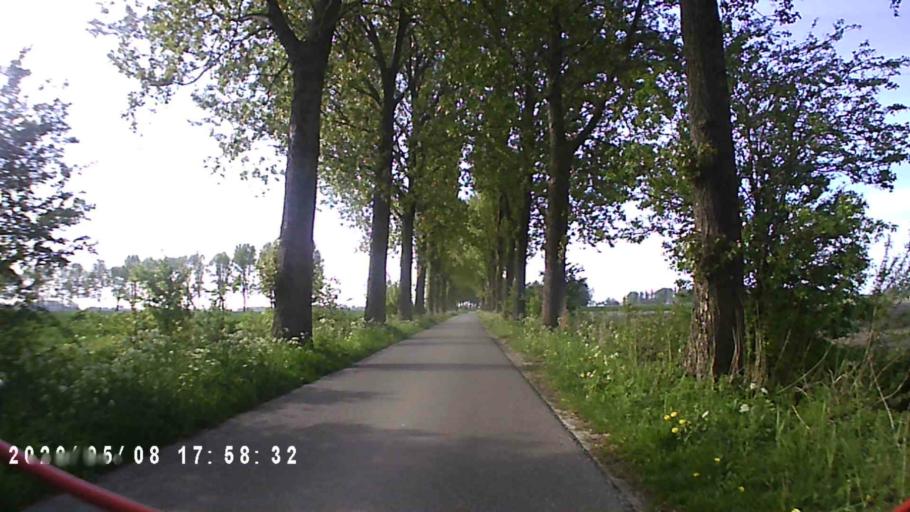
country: NL
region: Groningen
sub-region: Gemeente Winsum
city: Winsum
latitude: 53.3709
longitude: 6.4833
